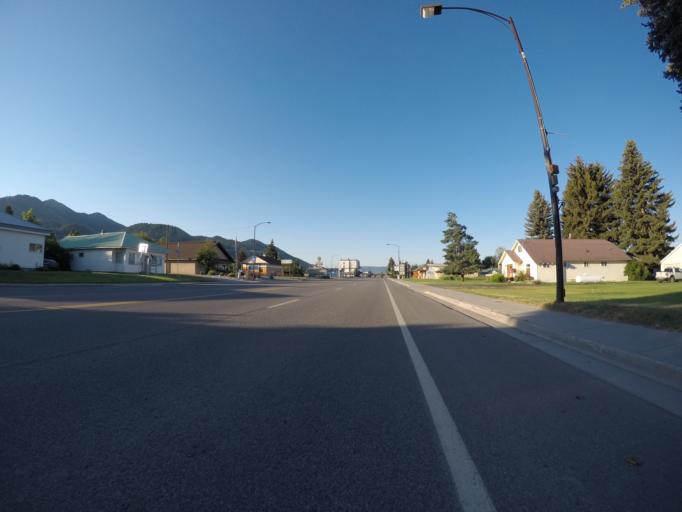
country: US
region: Wyoming
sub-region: Lincoln County
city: Afton
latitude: 42.7287
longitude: -110.9334
